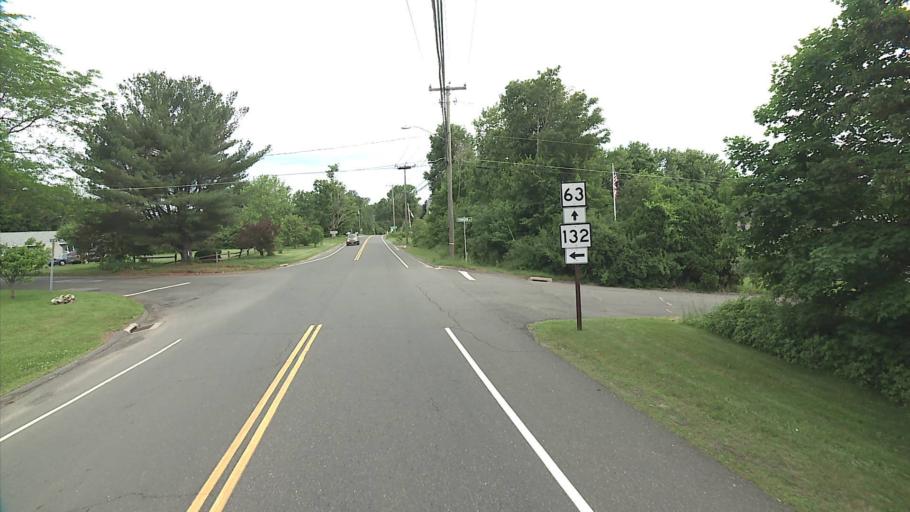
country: US
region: Connecticut
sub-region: Litchfield County
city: Watertown
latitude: 41.6453
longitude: -73.1485
